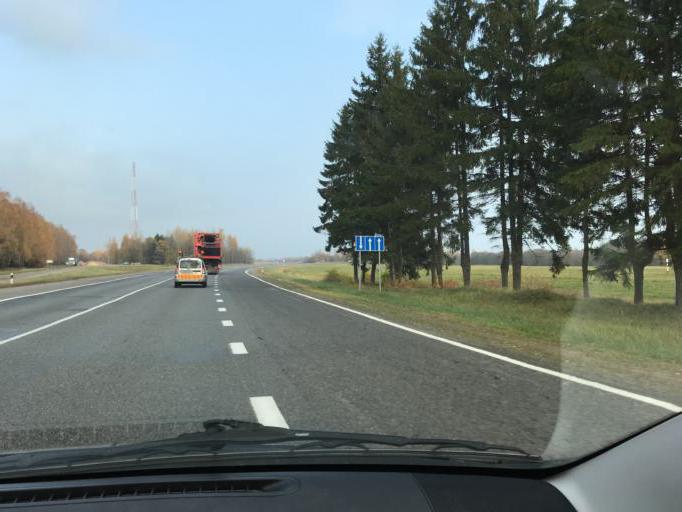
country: BY
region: Vitebsk
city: Syanno
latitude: 55.1435
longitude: 29.8295
